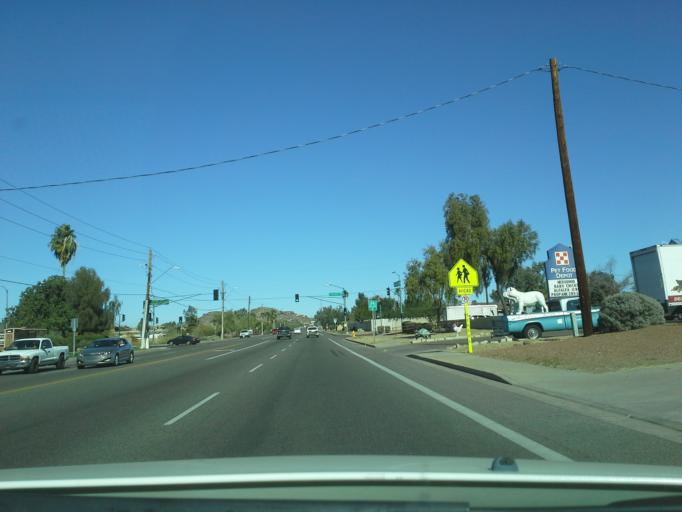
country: US
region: Arizona
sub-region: Maricopa County
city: Paradise Valley
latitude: 33.6468
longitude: -112.0308
